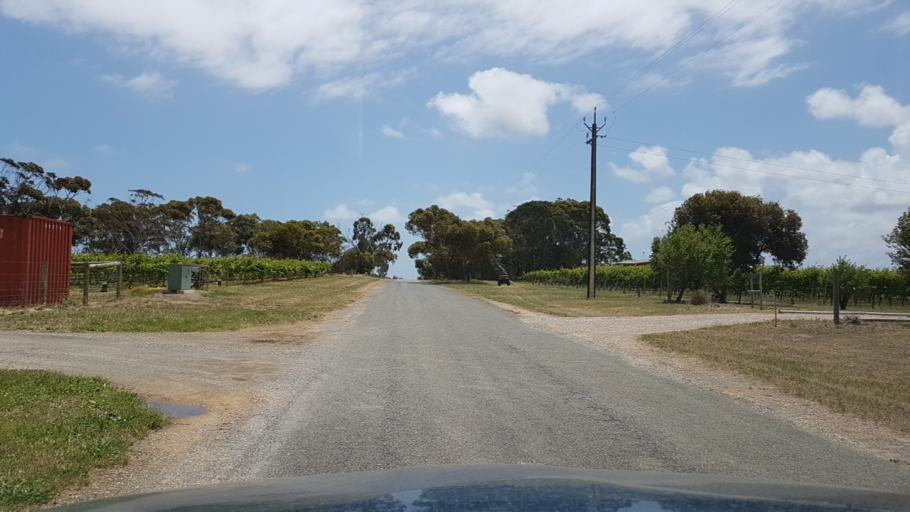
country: AU
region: South Australia
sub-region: Onkaparinga
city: McLaren Vale
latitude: -35.2491
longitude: 138.5332
